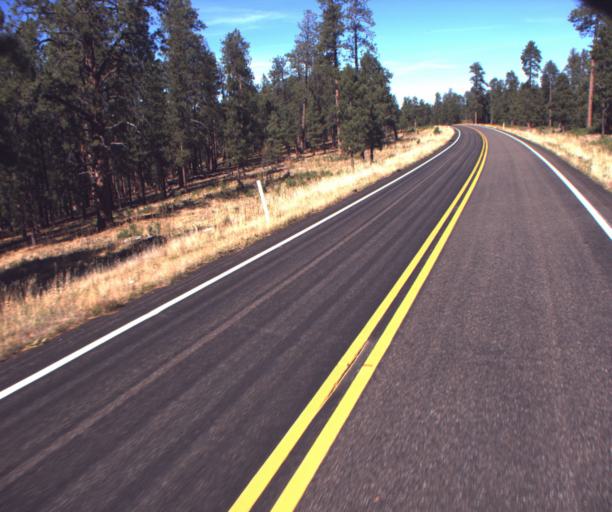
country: US
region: Arizona
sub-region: Coconino County
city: Fredonia
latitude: 36.6931
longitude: -112.2145
